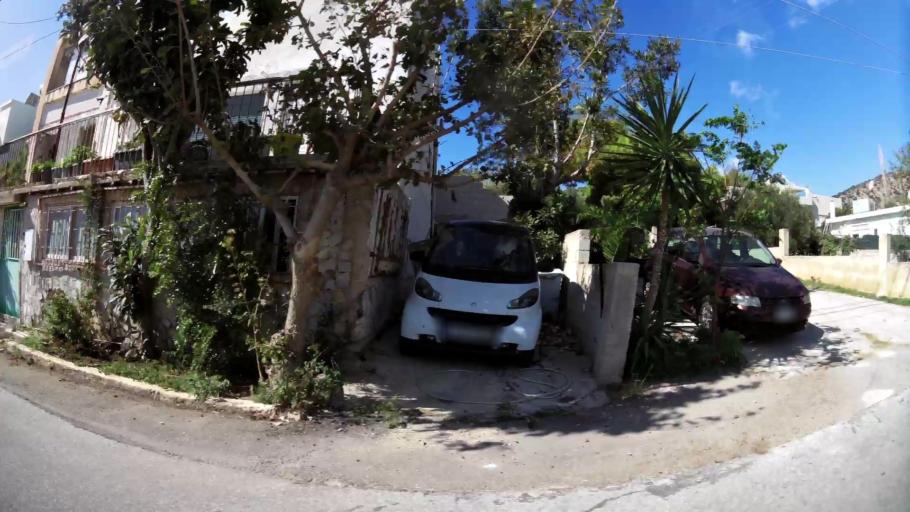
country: GR
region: Attica
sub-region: Nomarchia Anatolikis Attikis
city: Vari
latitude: 37.8413
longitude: 23.7964
